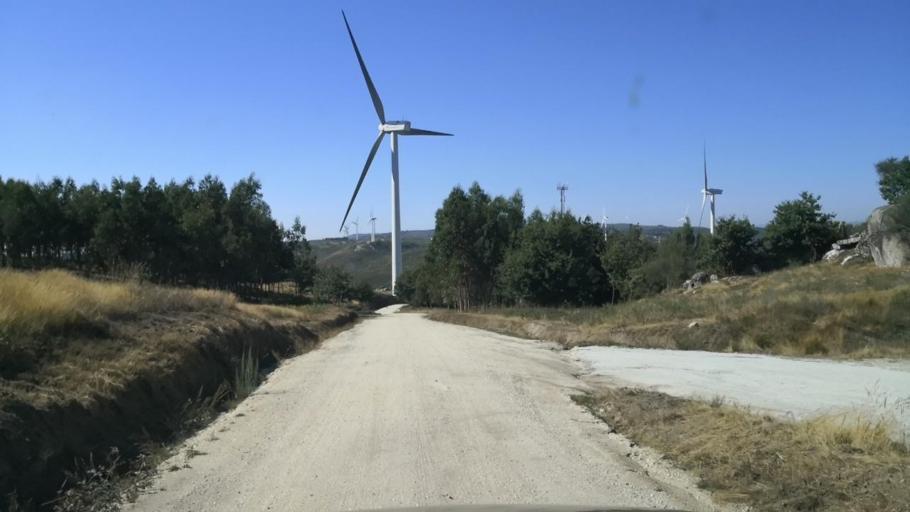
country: PT
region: Braga
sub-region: Cabeceiras de Basto
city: Refojos de Basto
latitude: 41.4910
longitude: -8.0700
